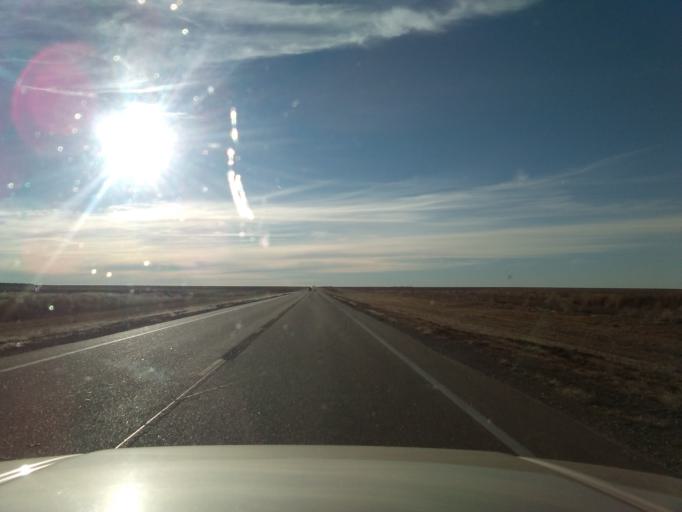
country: US
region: Kansas
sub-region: Sheridan County
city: Hoxie
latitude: 39.5343
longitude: -100.5907
